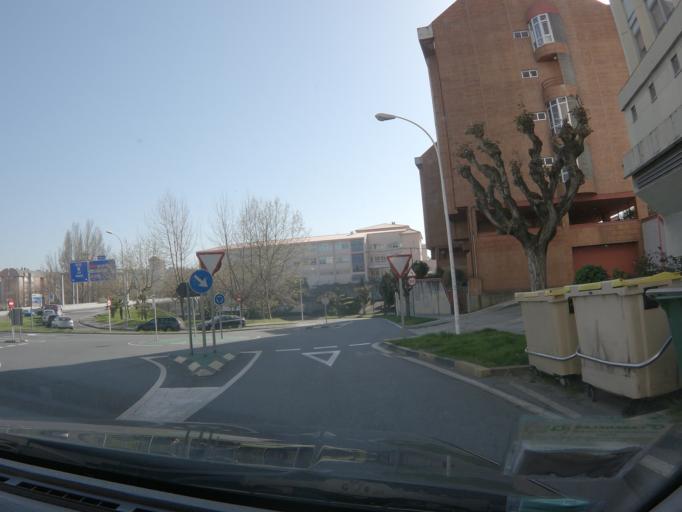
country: ES
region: Galicia
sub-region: Provincia da Coruna
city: A Coruna
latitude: 43.3503
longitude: -8.4105
